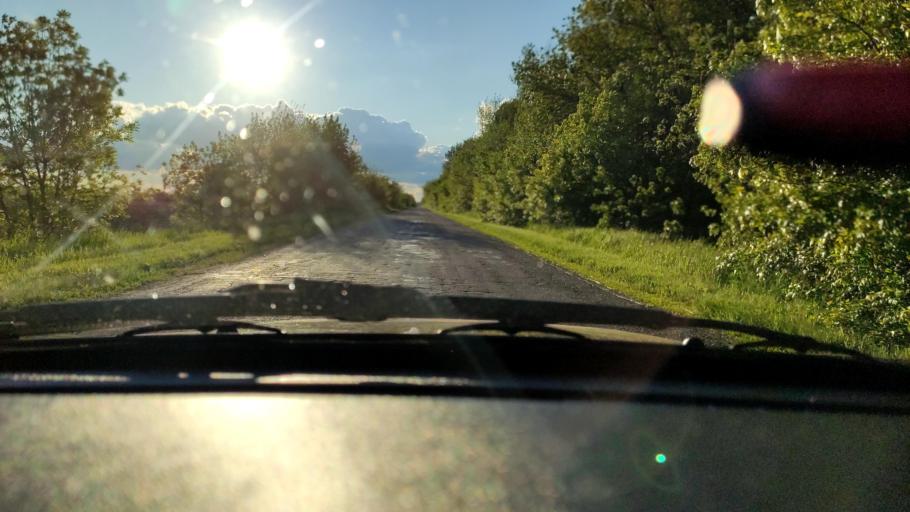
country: RU
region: Voronezj
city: Uryv-Pokrovka
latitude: 51.1362
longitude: 39.0871
